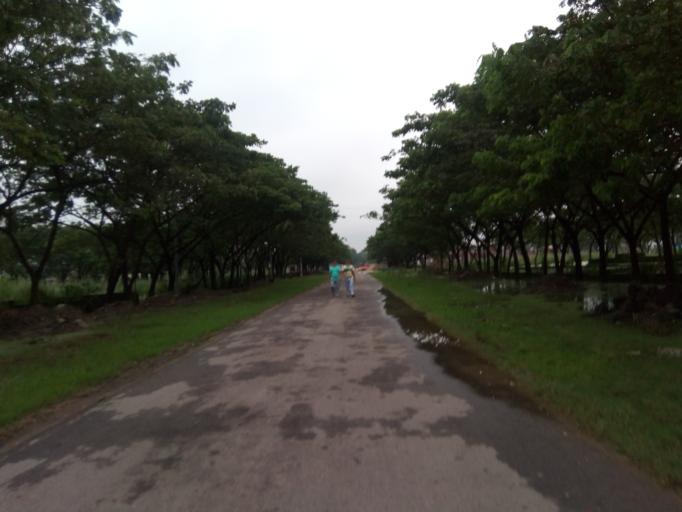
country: BD
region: Dhaka
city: Tungi
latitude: 23.8479
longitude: 90.4258
